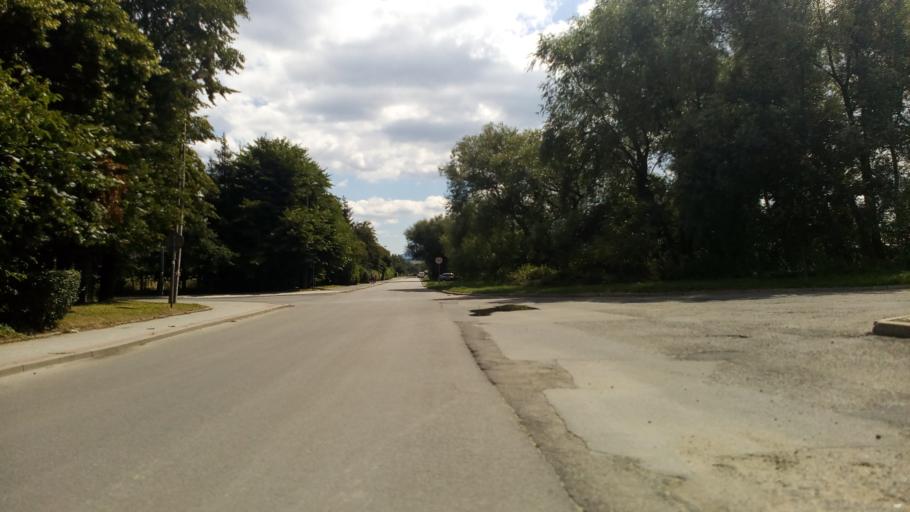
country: PL
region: Lesser Poland Voivodeship
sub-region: Powiat nowosadecki
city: Nowy Sacz
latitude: 49.6109
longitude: 20.6812
